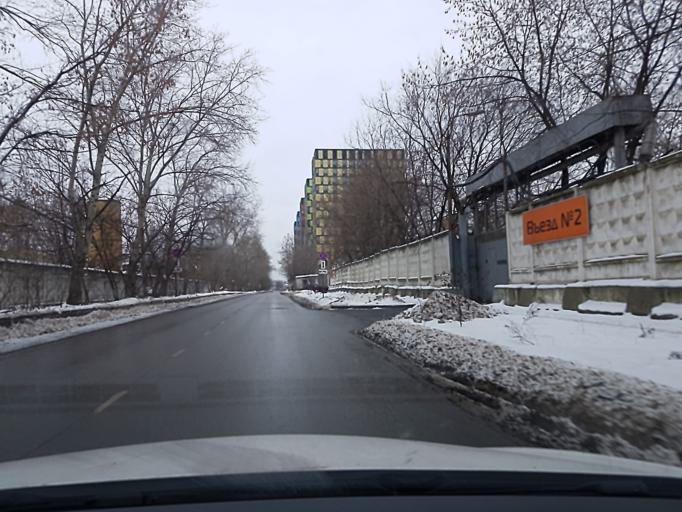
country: RU
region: Moskovskaya
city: Kozhukhovo
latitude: 55.6883
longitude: 37.6538
